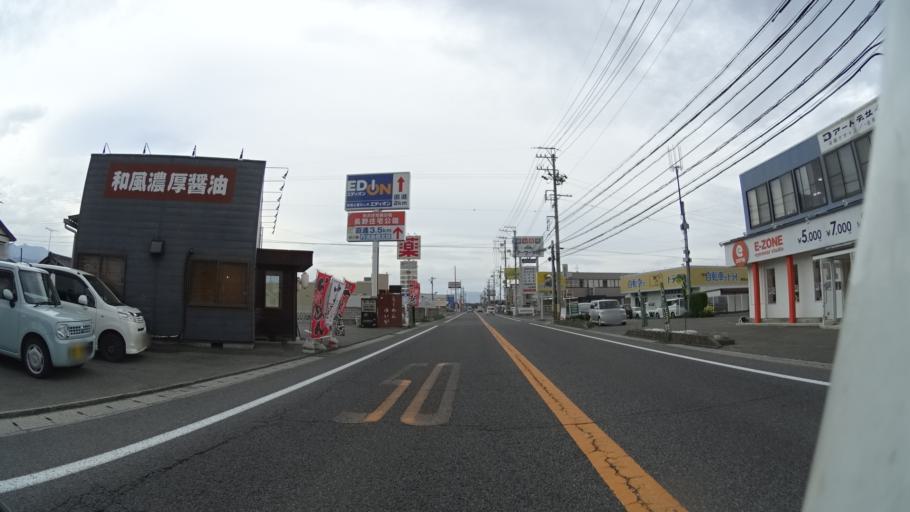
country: JP
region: Nagano
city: Nagano-shi
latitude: 36.5998
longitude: 138.1592
